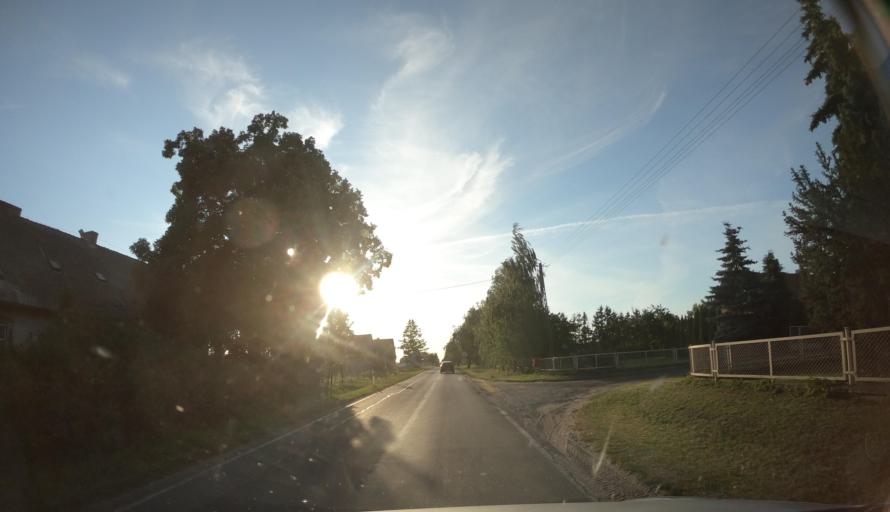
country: PL
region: Kujawsko-Pomorskie
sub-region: Powiat swiecki
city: Pruszcz
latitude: 53.2467
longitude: 18.2036
